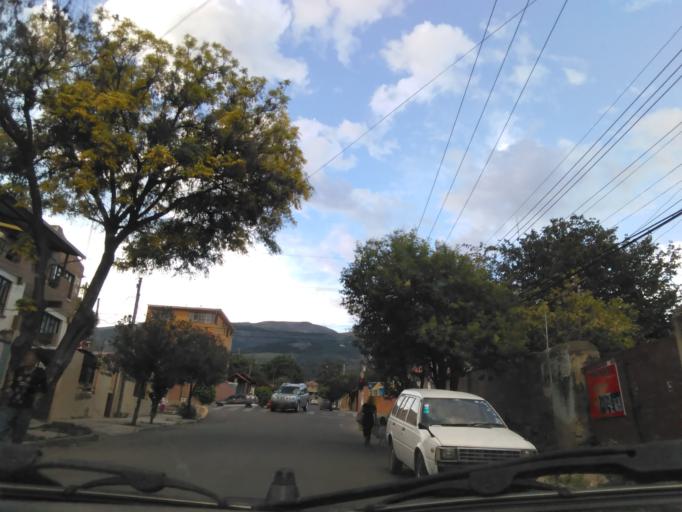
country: BO
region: Cochabamba
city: Cochabamba
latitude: -17.3673
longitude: -66.1531
